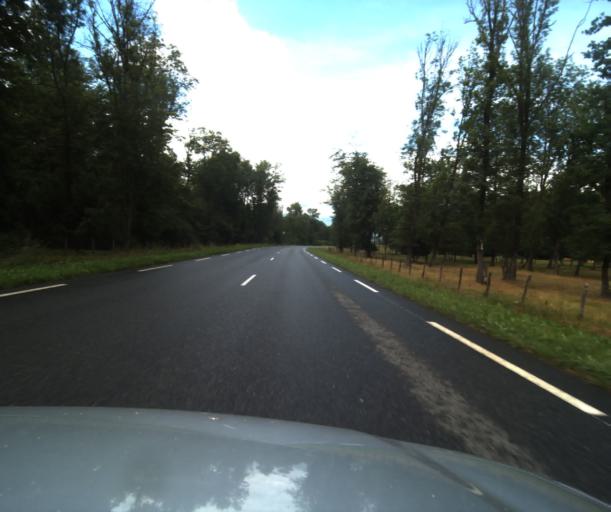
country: FR
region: Midi-Pyrenees
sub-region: Departement des Hautes-Pyrenees
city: Pierrefitte-Nestalas
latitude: 42.9743
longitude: -0.0662
